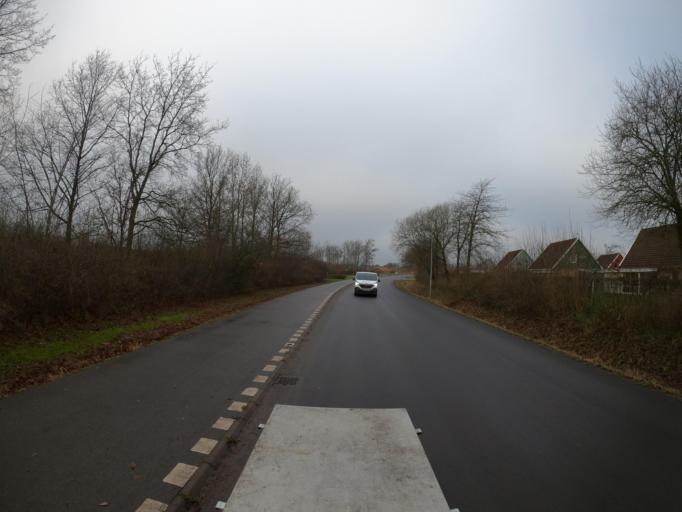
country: SE
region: Skane
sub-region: Svedala Kommun
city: Svedala
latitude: 55.5185
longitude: 13.2325
